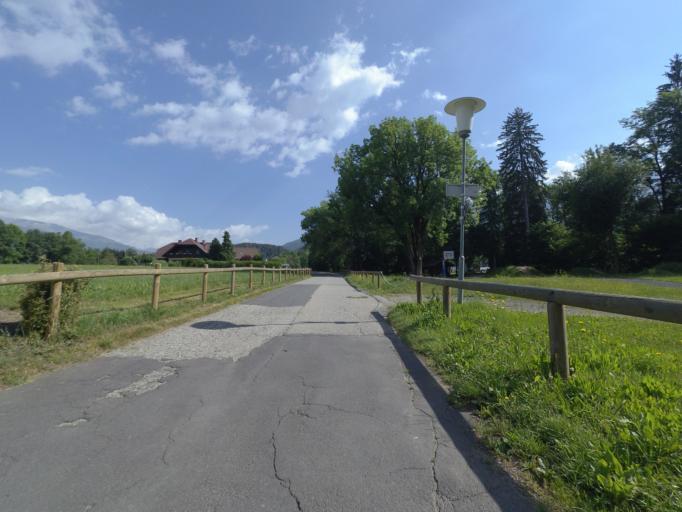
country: AT
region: Carinthia
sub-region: Politischer Bezirk Spittal an der Drau
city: Seeboden
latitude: 46.8161
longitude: 13.5277
